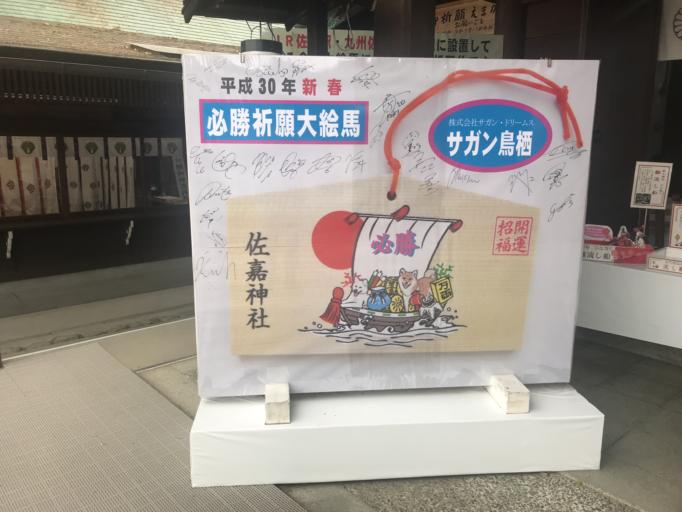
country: JP
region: Saga Prefecture
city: Saga-shi
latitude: 33.2518
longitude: 130.3025
